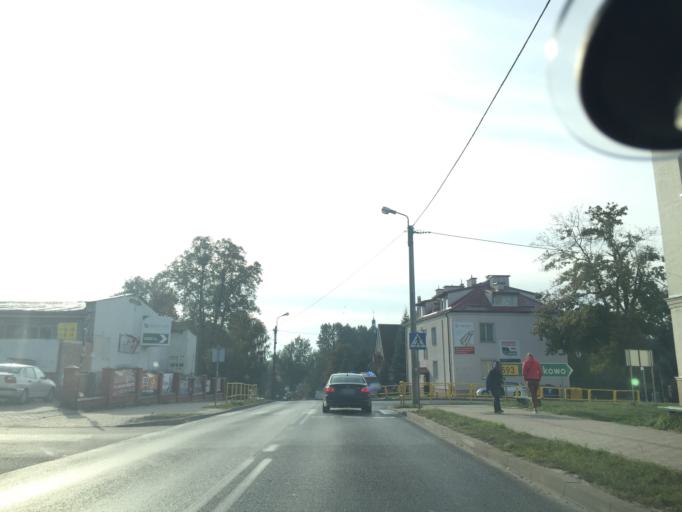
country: PL
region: Warmian-Masurian Voivodeship
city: Dobre Miasto
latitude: 53.9897
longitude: 20.3951
